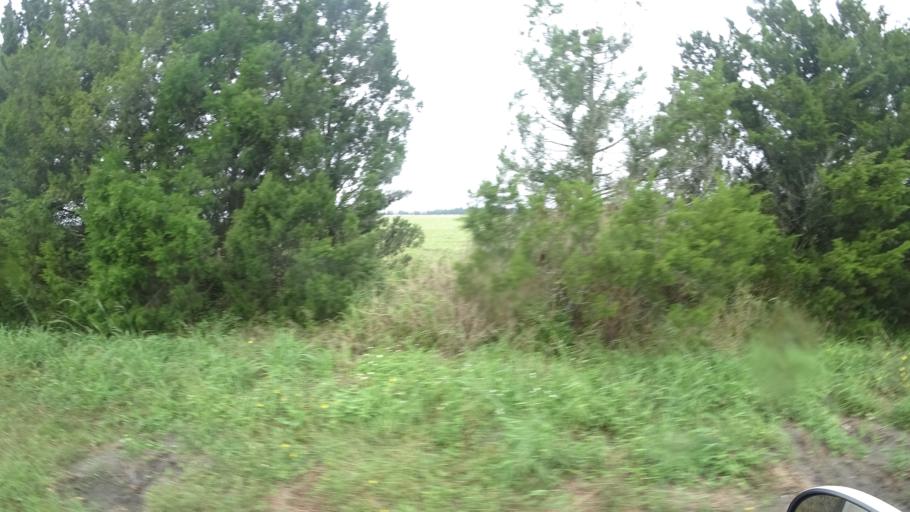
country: US
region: Florida
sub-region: Sarasota County
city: Warm Mineral Springs
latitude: 27.3089
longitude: -82.1496
